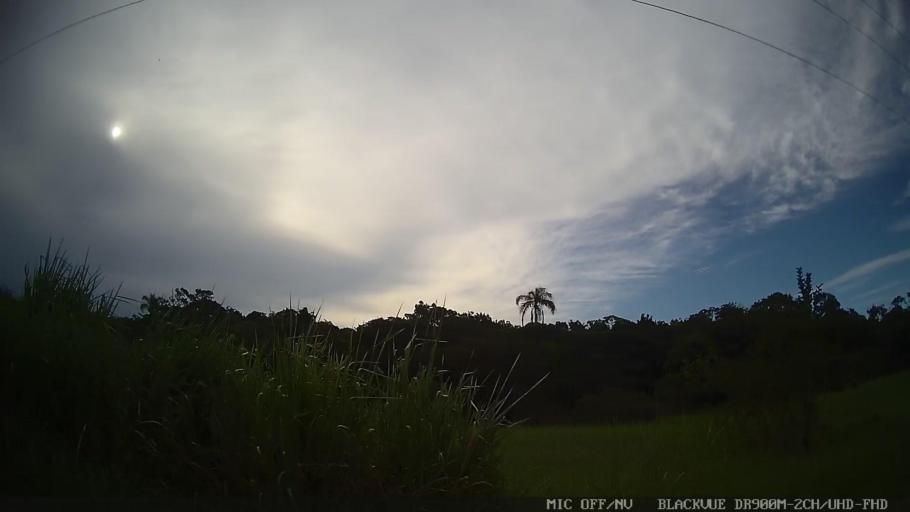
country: BR
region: Sao Paulo
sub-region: Iguape
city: Iguape
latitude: -24.6559
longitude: -47.4083
